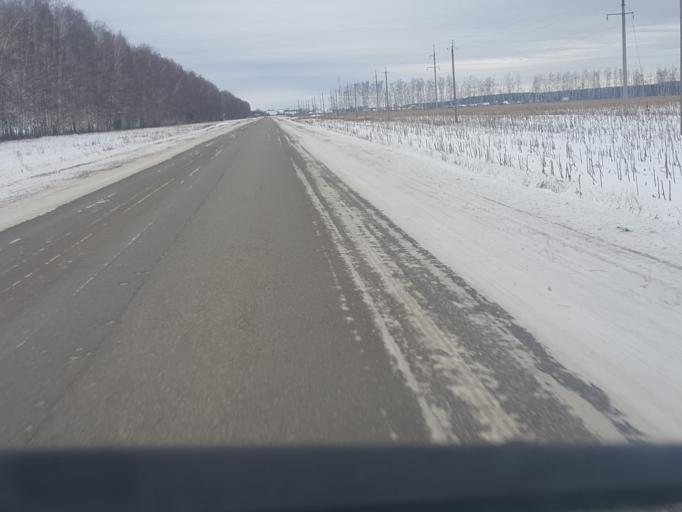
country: RU
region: Tambov
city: Rasskazovo
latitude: 52.8171
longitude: 41.7959
